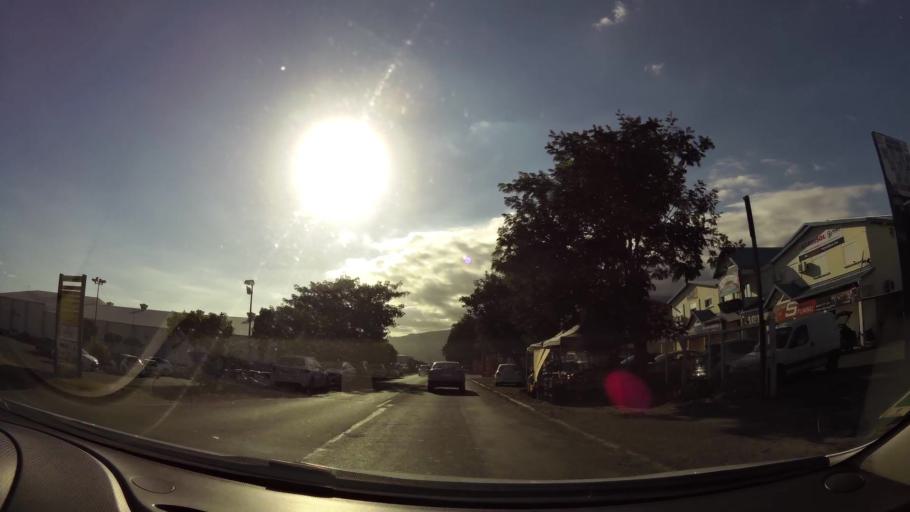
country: RE
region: Reunion
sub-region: Reunion
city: Saint-Louis
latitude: -21.2913
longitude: 55.4006
